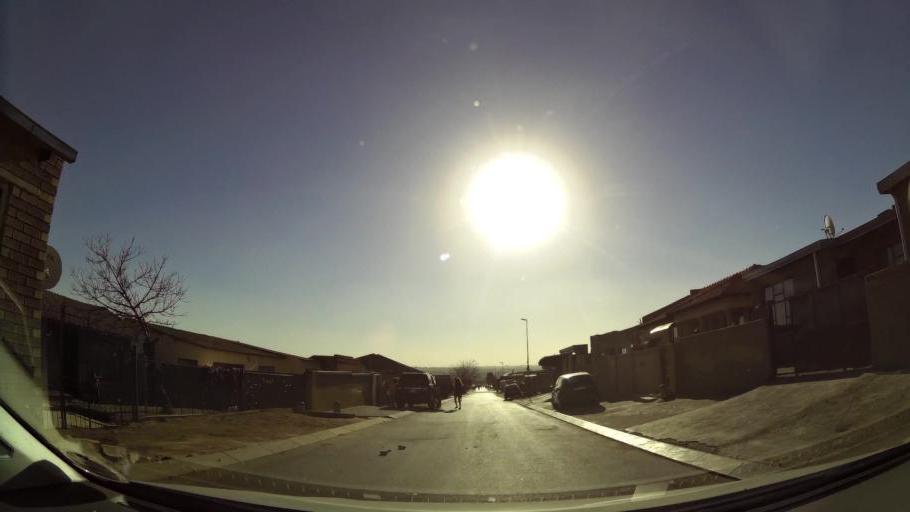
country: ZA
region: Gauteng
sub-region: Ekurhuleni Metropolitan Municipality
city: Tembisa
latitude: -26.0270
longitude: 28.2126
